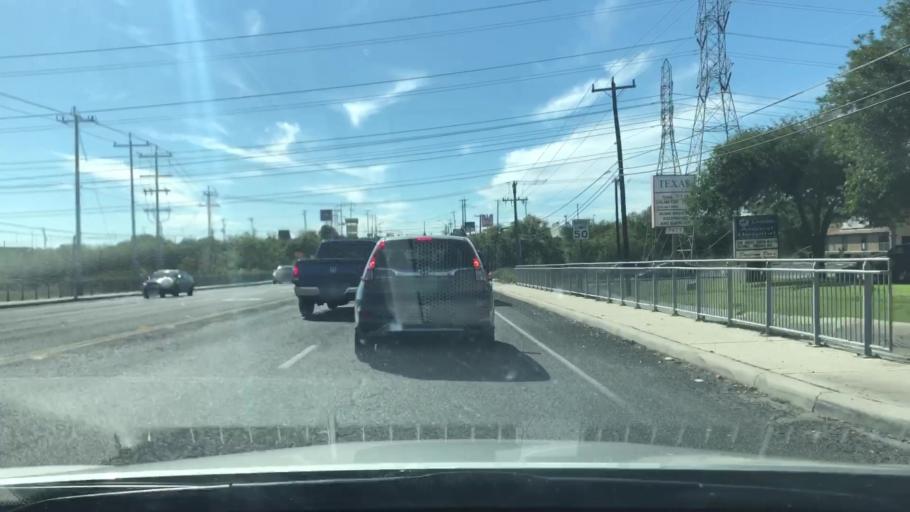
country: US
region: Texas
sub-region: Bexar County
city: Converse
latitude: 29.4931
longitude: -98.3317
